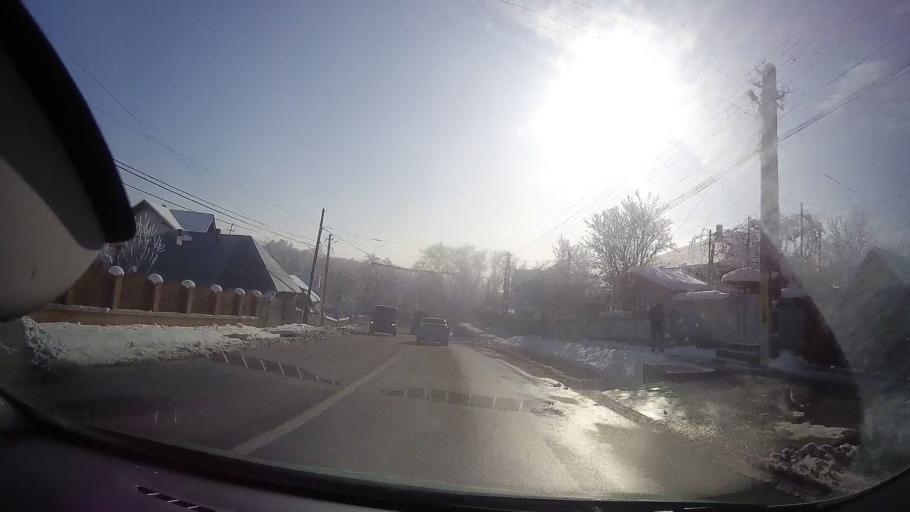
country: RO
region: Iasi
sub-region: Comuna Motca
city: Motca
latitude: 47.2367
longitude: 26.6034
